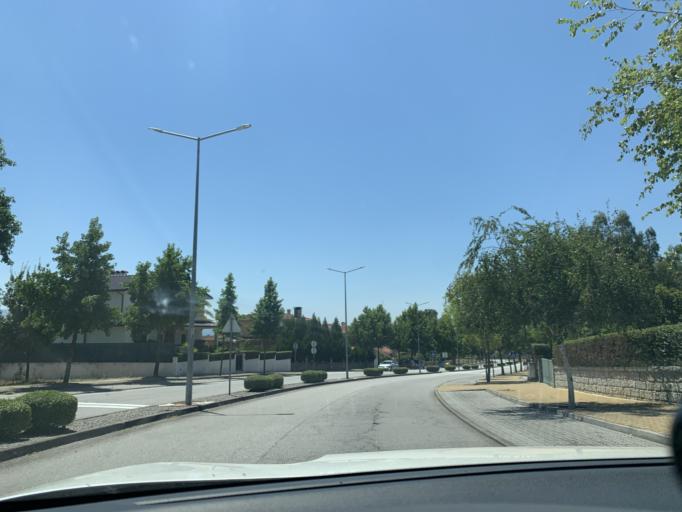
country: PT
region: Viseu
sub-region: Mangualde
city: Mangualde
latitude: 40.5946
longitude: -7.7575
